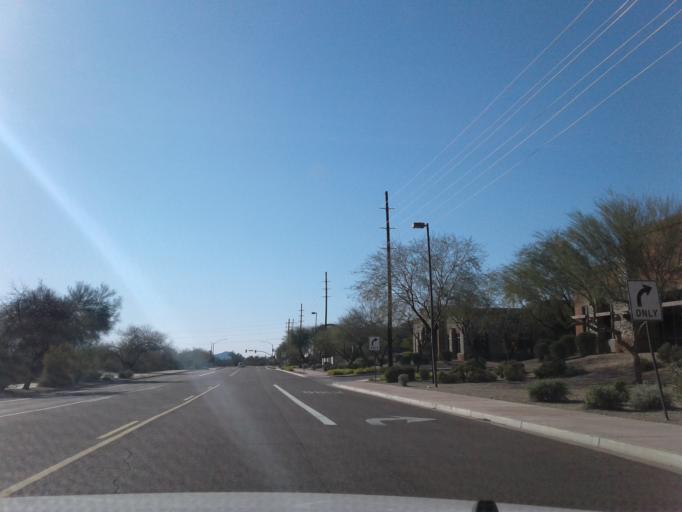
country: US
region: Arizona
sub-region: Maricopa County
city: Carefree
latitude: 33.6842
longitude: -111.9218
